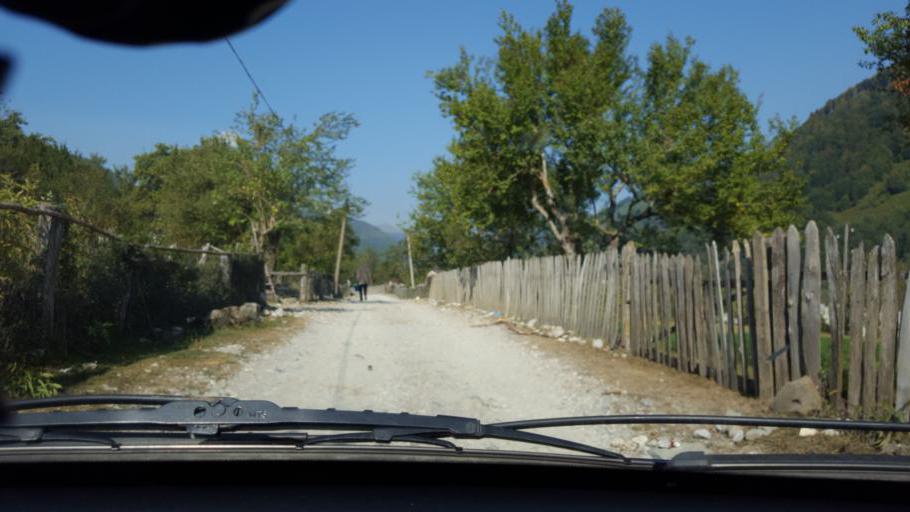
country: ME
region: Andrijevica
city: Andrijevica
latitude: 42.5903
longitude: 19.6914
